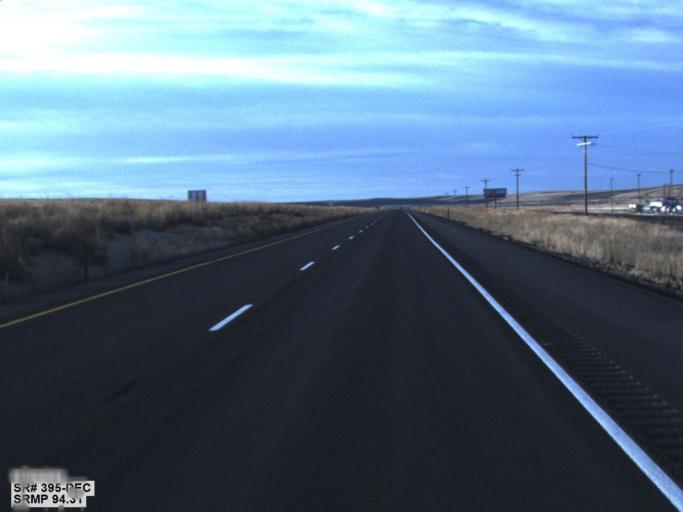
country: US
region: Washington
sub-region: Adams County
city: Ritzville
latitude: 47.0929
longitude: -118.4099
